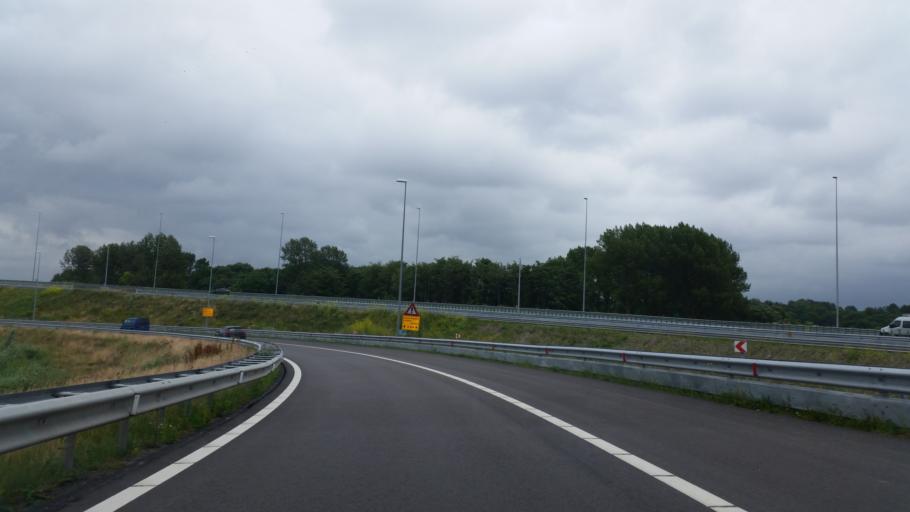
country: NL
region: North Holland
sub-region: Gemeente Naarden
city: Naarden
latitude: 52.3412
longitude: 5.1745
